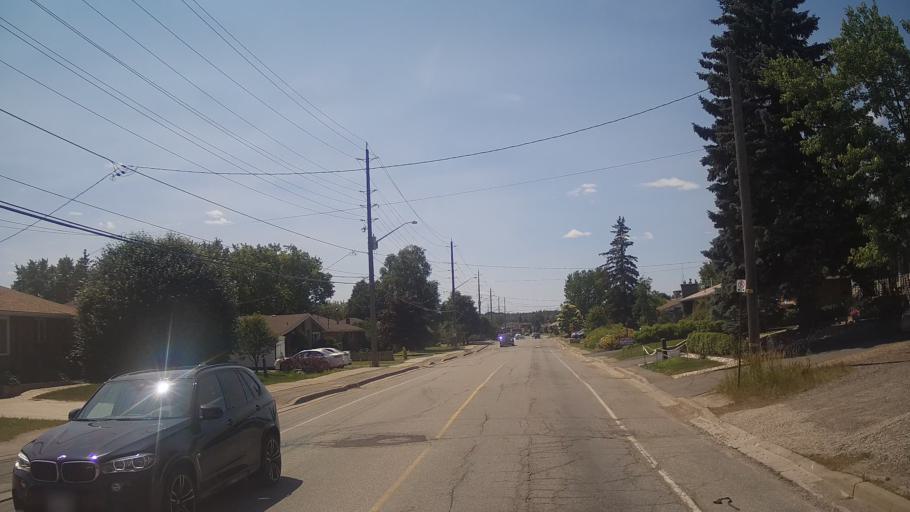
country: CA
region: Ontario
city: Greater Sudbury
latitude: 46.4597
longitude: -81.0223
